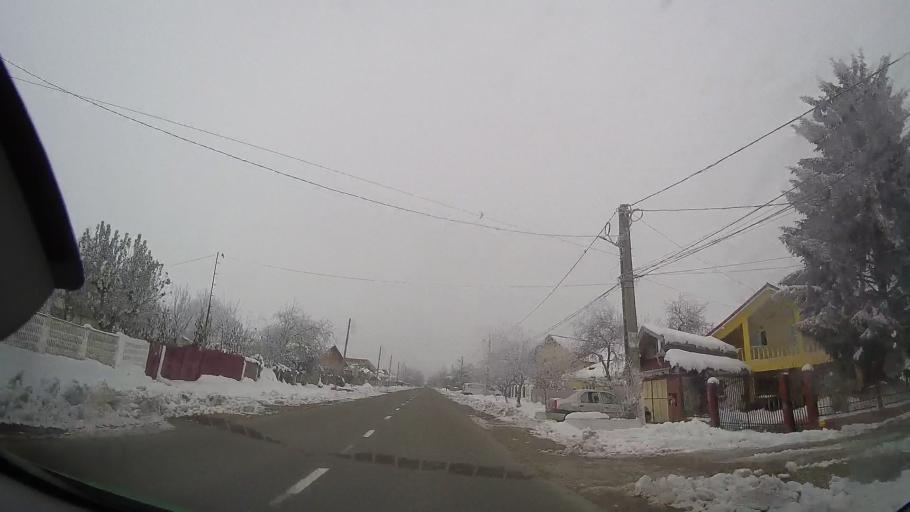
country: RO
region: Neamt
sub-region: Comuna Horia
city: Cotu Vames
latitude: 46.8980
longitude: 26.9580
